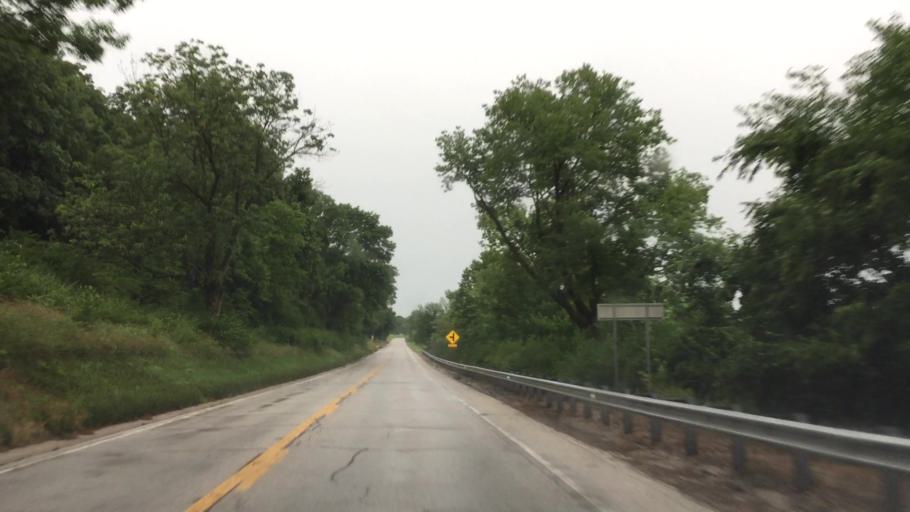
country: US
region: Illinois
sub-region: Hancock County
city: Nauvoo
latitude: 40.5330
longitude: -91.3758
